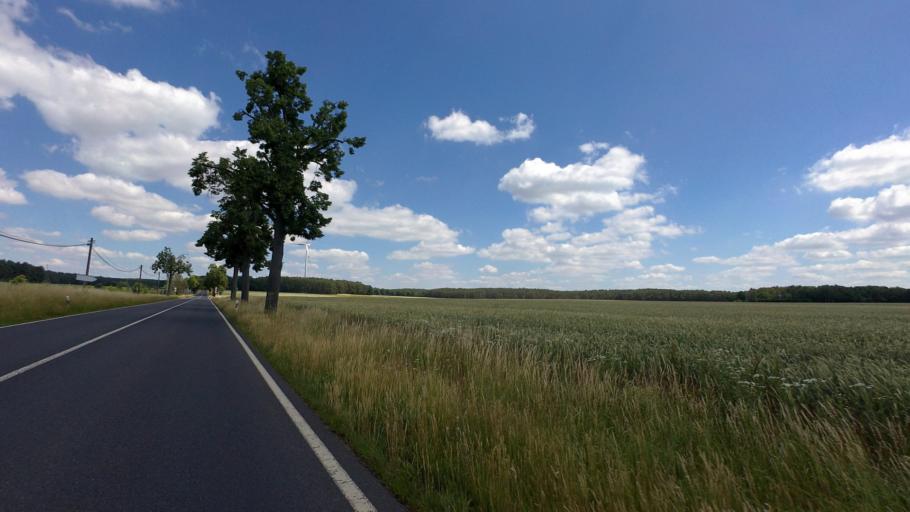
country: DE
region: Brandenburg
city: Sonnewalde
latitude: 51.7126
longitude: 13.6682
